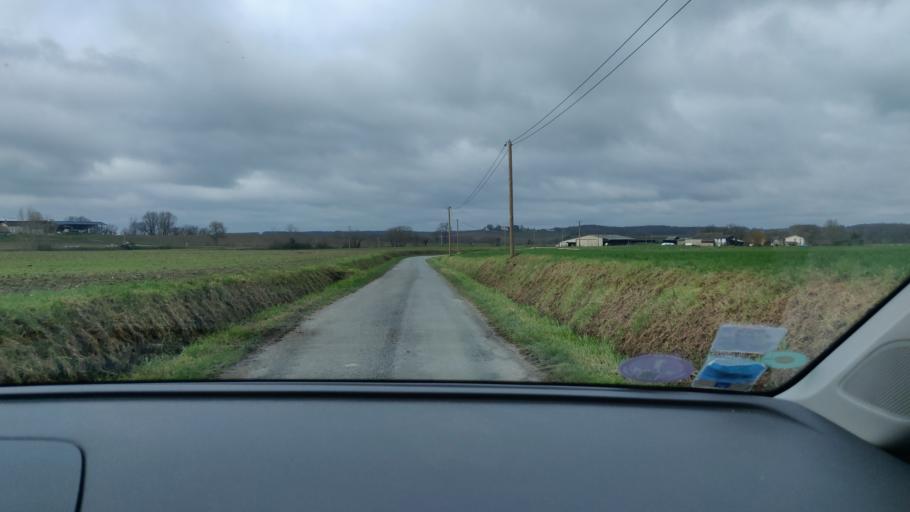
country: FR
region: Aquitaine
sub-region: Departement du Lot-et-Garonne
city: Saint-Hilaire
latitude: 44.5734
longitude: 0.7245
